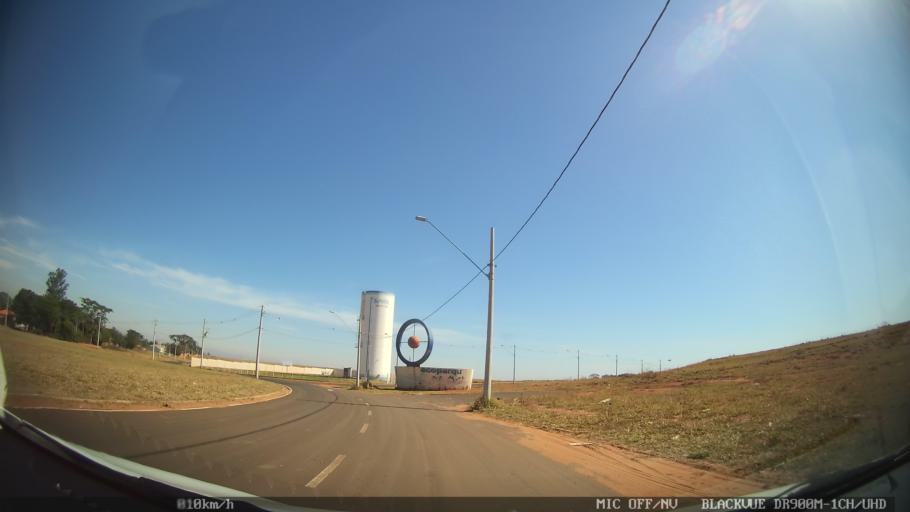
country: BR
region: Sao Paulo
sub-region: Sao Jose Do Rio Preto
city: Sao Jose do Rio Preto
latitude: -20.7264
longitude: -49.4383
